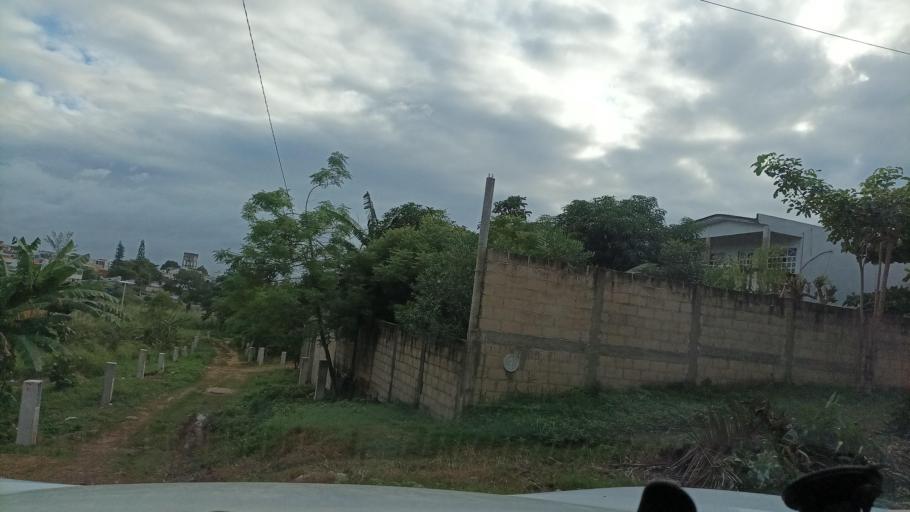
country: MX
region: Veracruz
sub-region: Cosoleacaque
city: Hermenegildo J. Aldana
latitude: 17.9963
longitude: -94.6096
